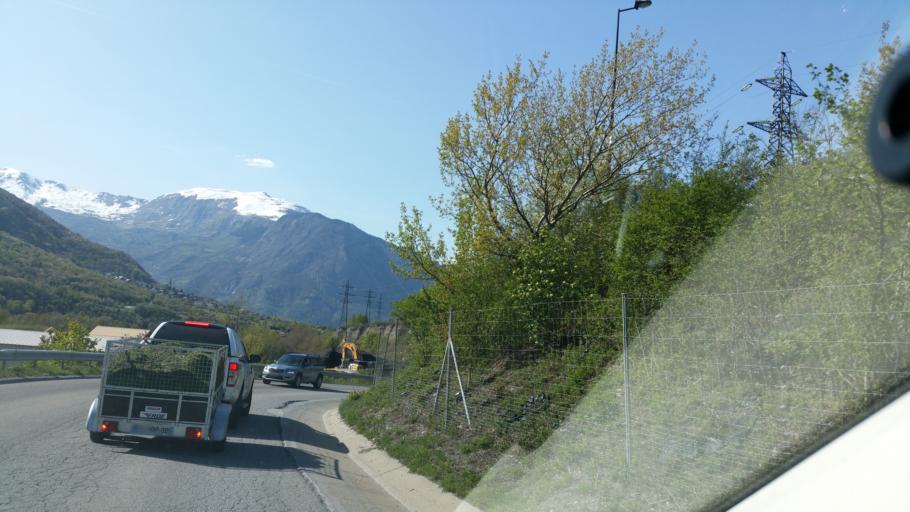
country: FR
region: Rhone-Alpes
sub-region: Departement de la Savoie
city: Villargondran
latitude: 45.2516
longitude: 6.3958
